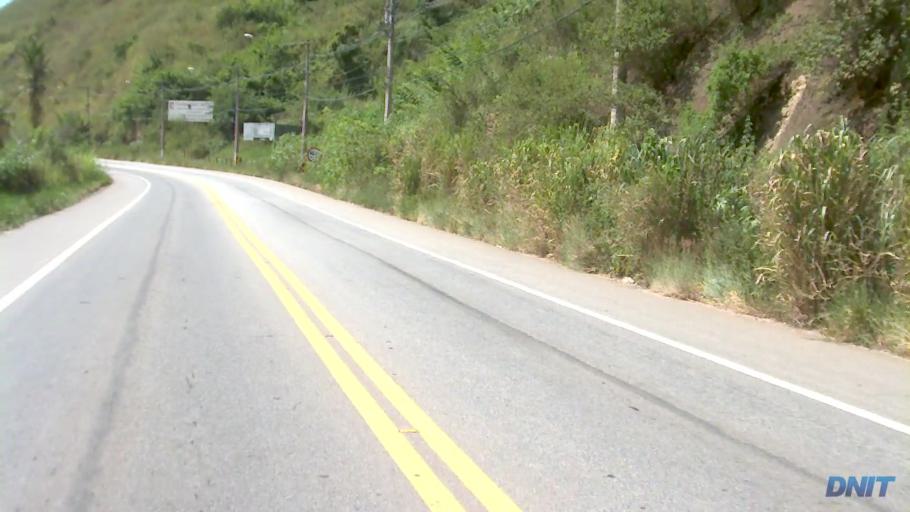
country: BR
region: Minas Gerais
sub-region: Timoteo
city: Timoteo
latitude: -19.5426
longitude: -42.6738
